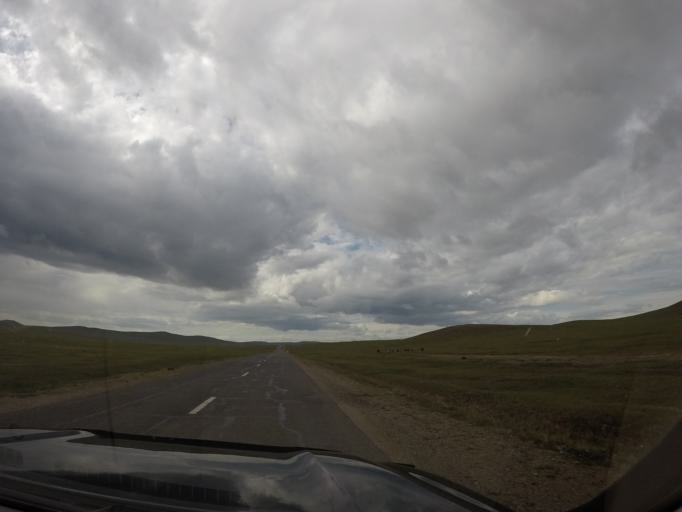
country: MN
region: Hentiy
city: Avraga
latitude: 47.5010
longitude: 109.4436
